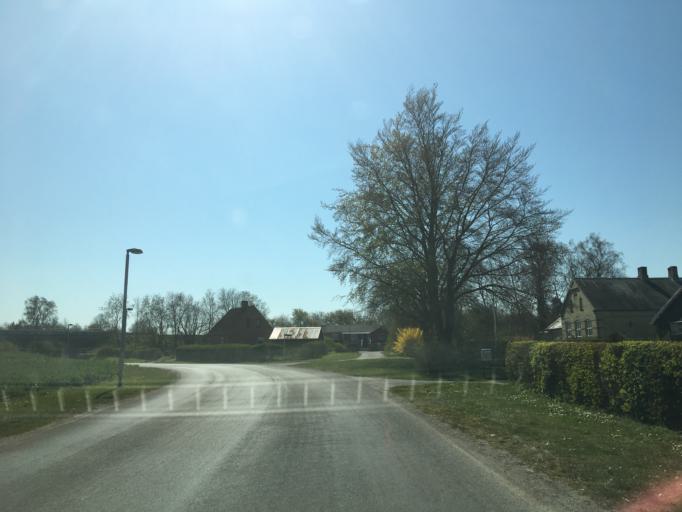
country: DK
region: Zealand
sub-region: Guldborgsund Kommune
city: Nykobing Falster
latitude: 54.7471
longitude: 11.7808
